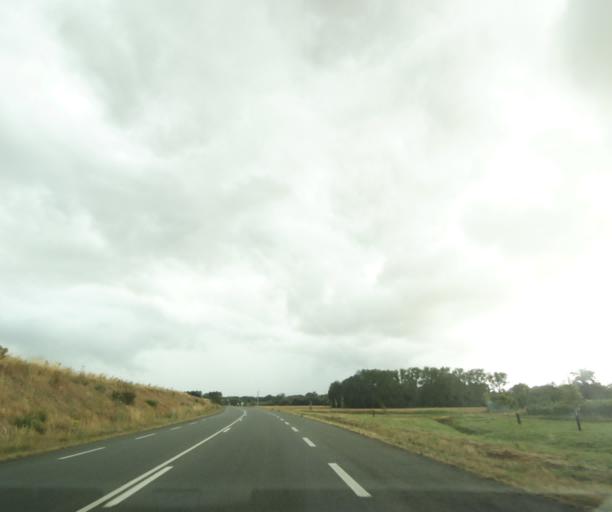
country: FR
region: Pays de la Loire
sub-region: Departement de la Vendee
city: Saint-Hilaire-de-Talmont
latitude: 46.4611
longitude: -1.6040
